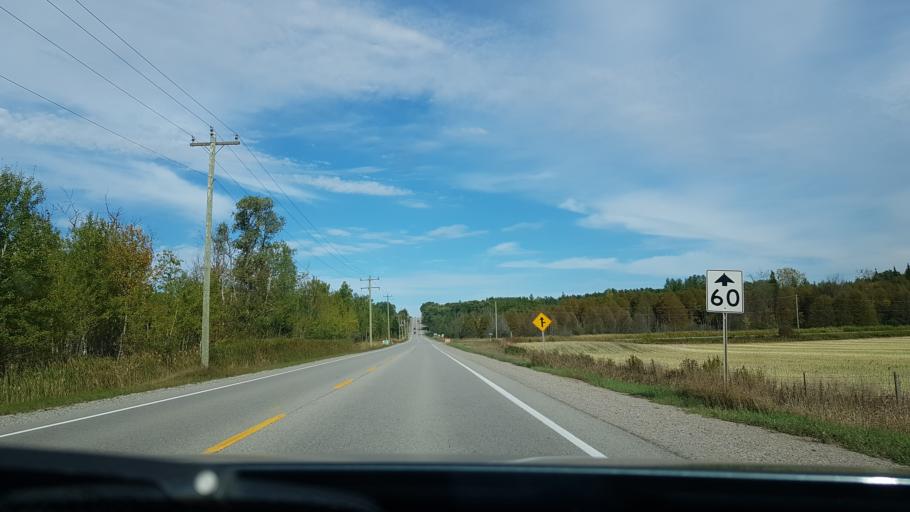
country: CA
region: Ontario
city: Angus
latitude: 44.4794
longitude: -79.8359
